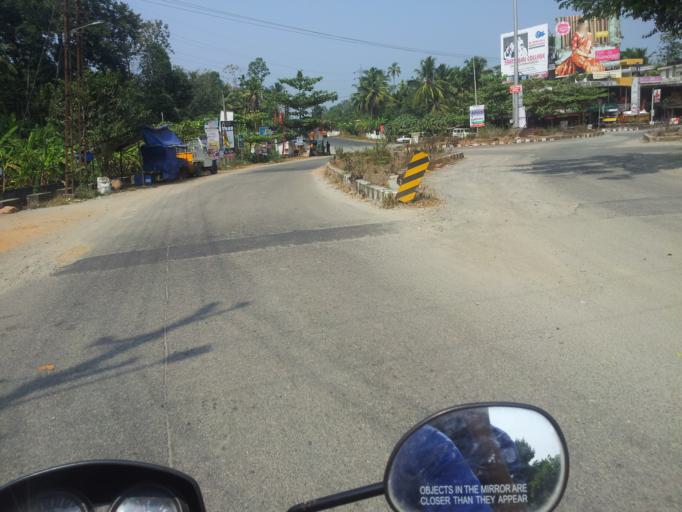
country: IN
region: Kerala
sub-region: Ernakulam
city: Muvattupuzha
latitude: 9.8861
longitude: 76.6959
